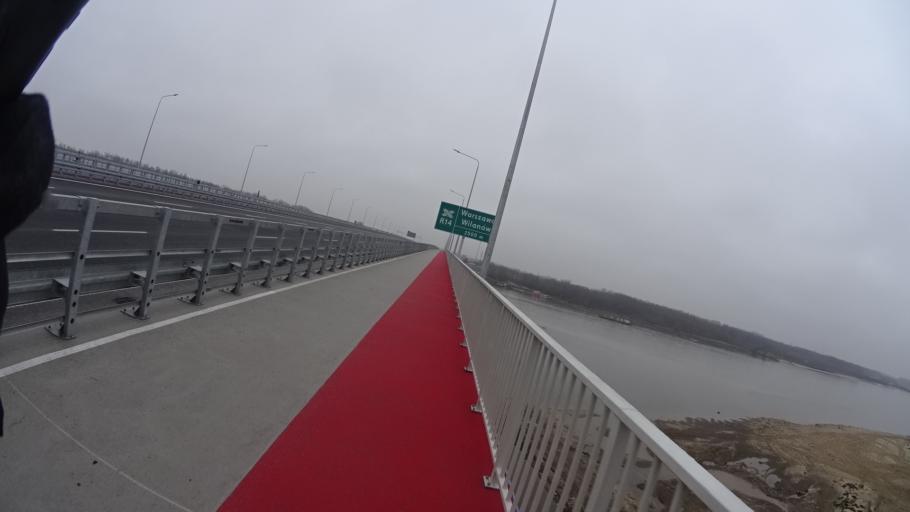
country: PL
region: Masovian Voivodeship
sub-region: Warszawa
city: Wawer
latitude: 52.1623
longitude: 21.1469
